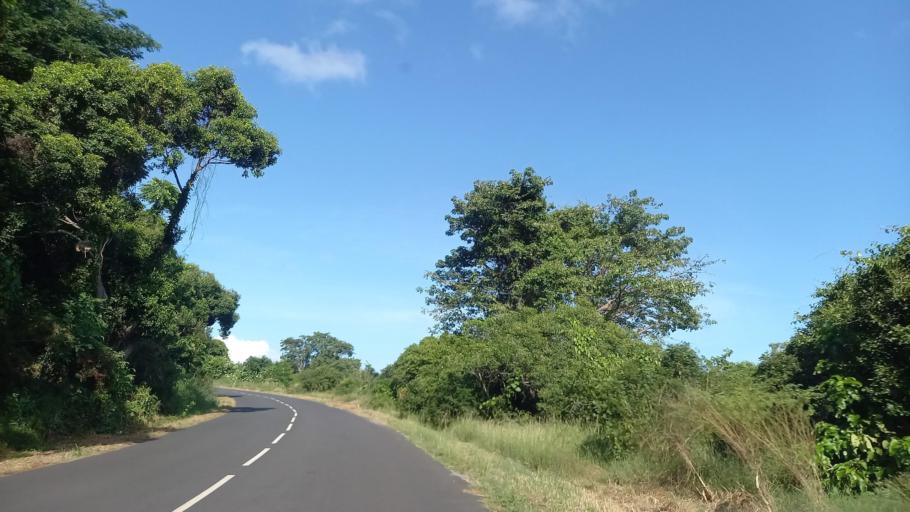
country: YT
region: Kani-Keli
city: Kani Keli
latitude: -12.9725
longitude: 45.1100
